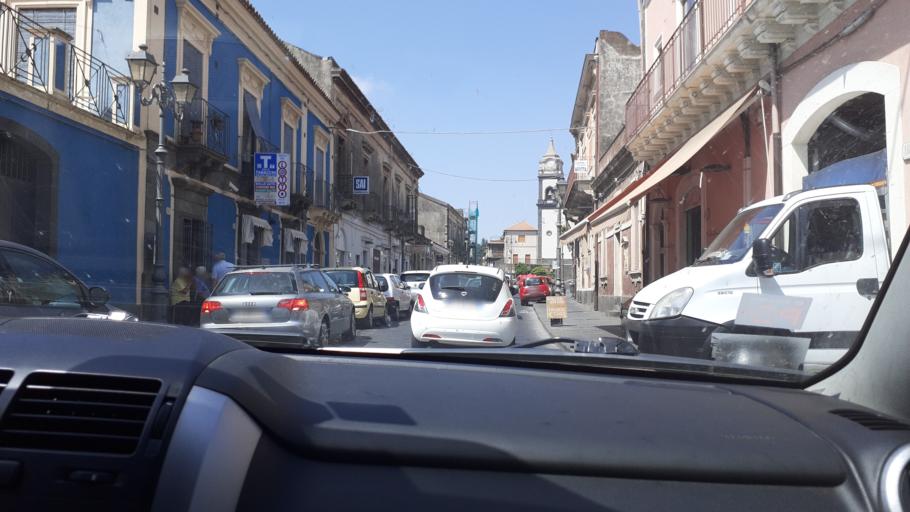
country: IT
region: Sicily
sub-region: Catania
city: Pedara
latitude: 37.6168
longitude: 15.0584
